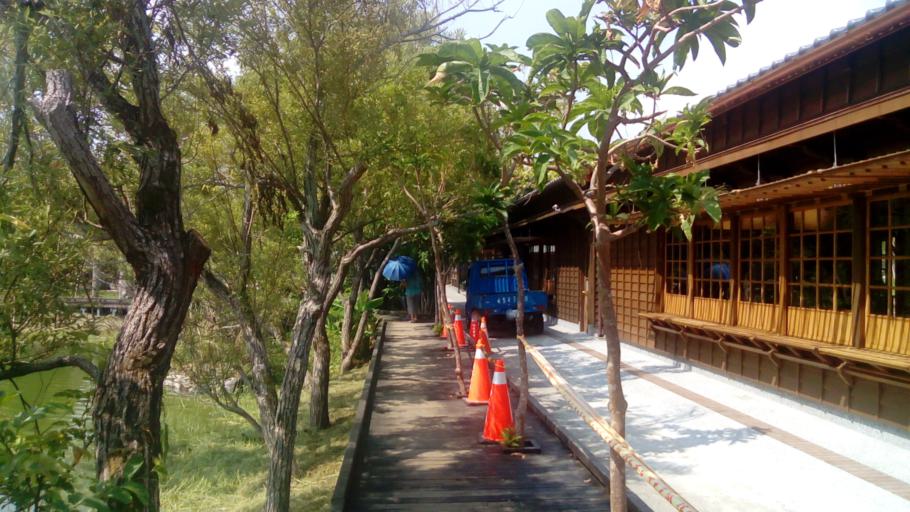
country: TW
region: Taiwan
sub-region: Yilan
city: Yilan
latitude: 24.6855
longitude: 121.7728
